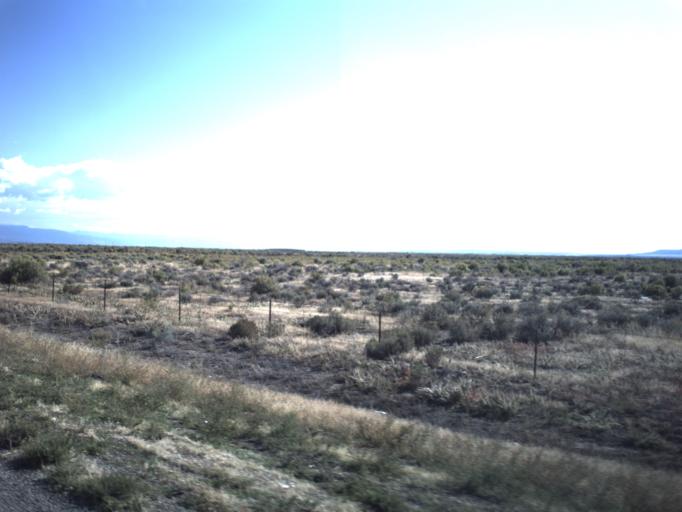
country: US
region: Utah
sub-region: Millard County
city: Delta
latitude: 39.2661
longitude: -112.4512
